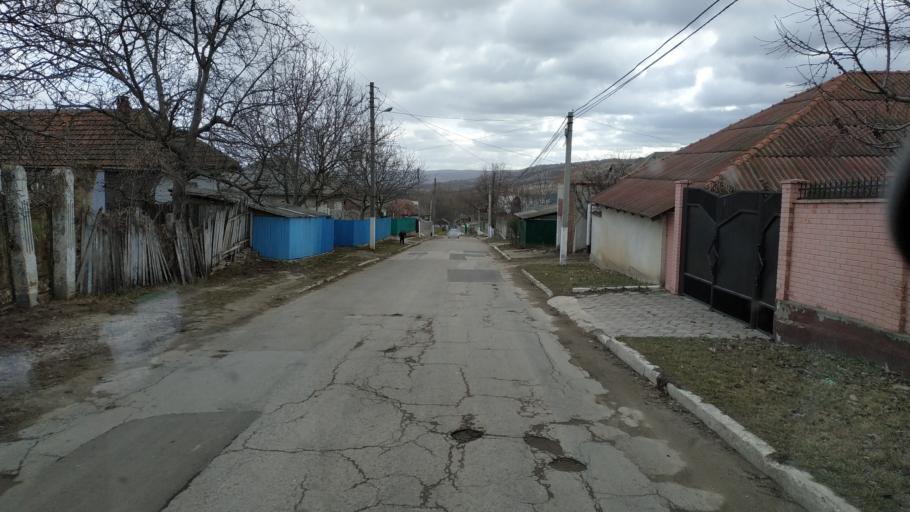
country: MD
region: Stinga Nistrului
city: Bucovat
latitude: 47.2331
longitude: 28.4229
